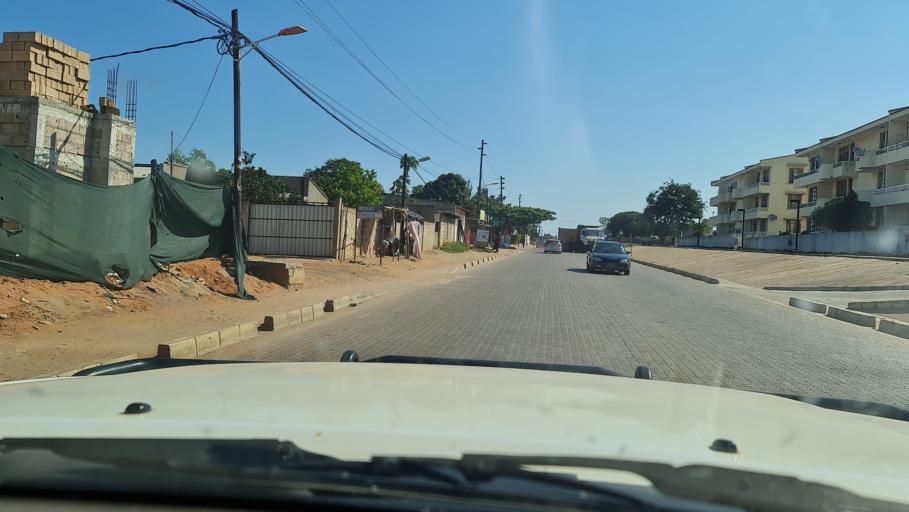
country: MZ
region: Maputo City
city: Maputo
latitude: -25.8392
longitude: 32.6364
